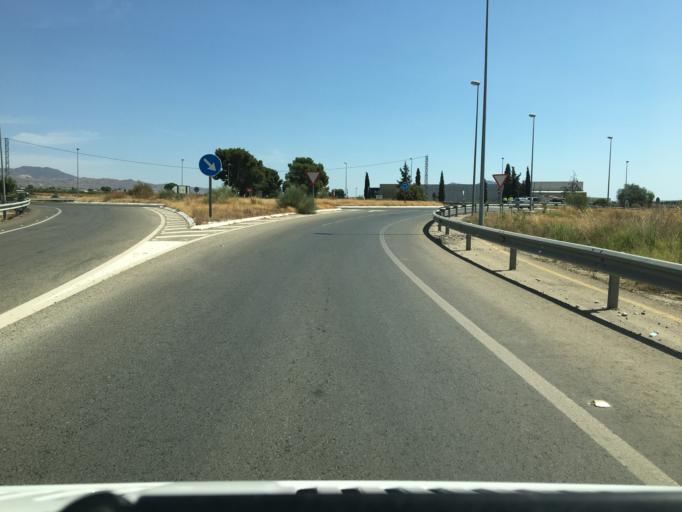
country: ES
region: Andalusia
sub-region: Provincia de Almeria
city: Huercal-Overa
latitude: 37.4155
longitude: -1.9253
